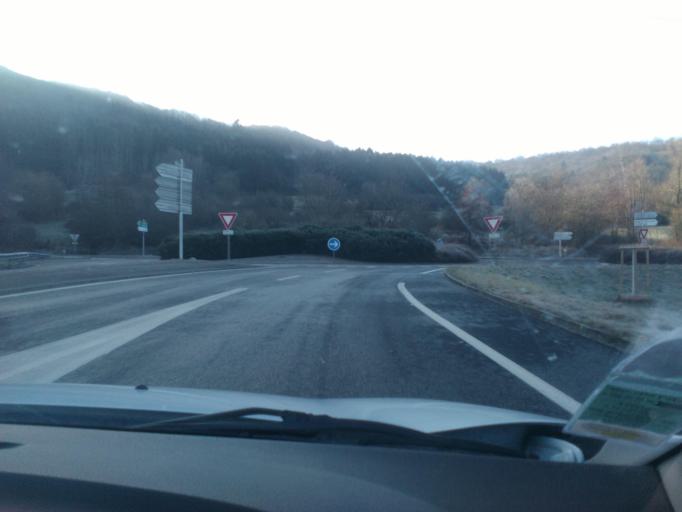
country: FR
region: Alsace
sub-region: Departement du Bas-Rhin
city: Russ
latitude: 48.4853
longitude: 7.2388
